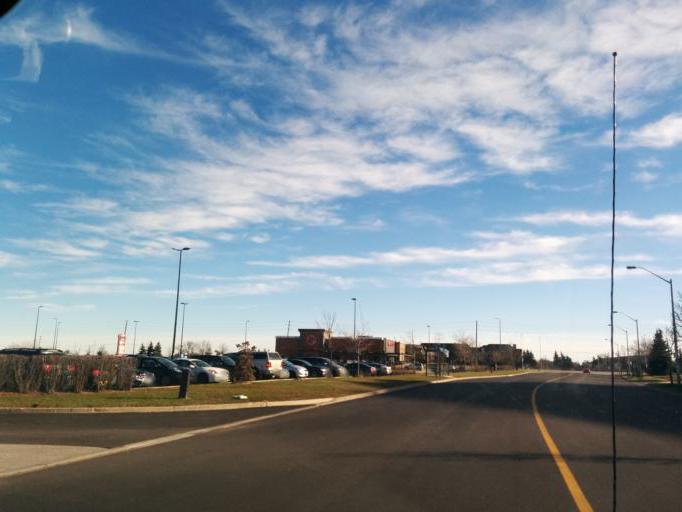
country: CA
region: Ontario
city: Oakville
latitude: 43.5086
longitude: -79.6695
